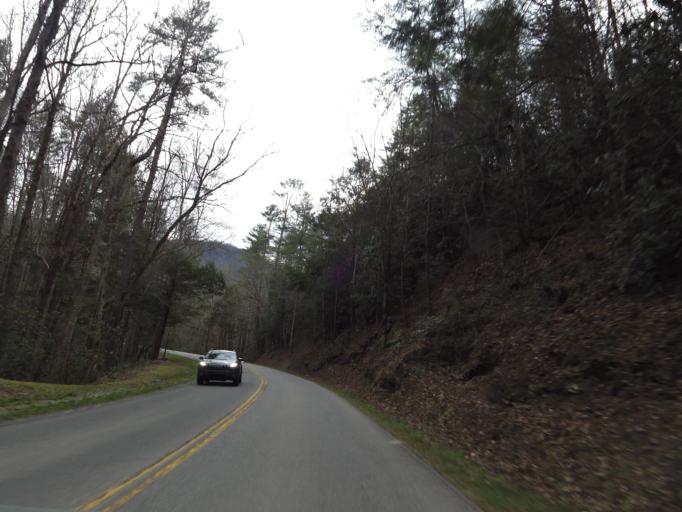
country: US
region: Tennessee
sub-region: Blount County
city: Wildwood
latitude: 35.6125
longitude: -83.7450
